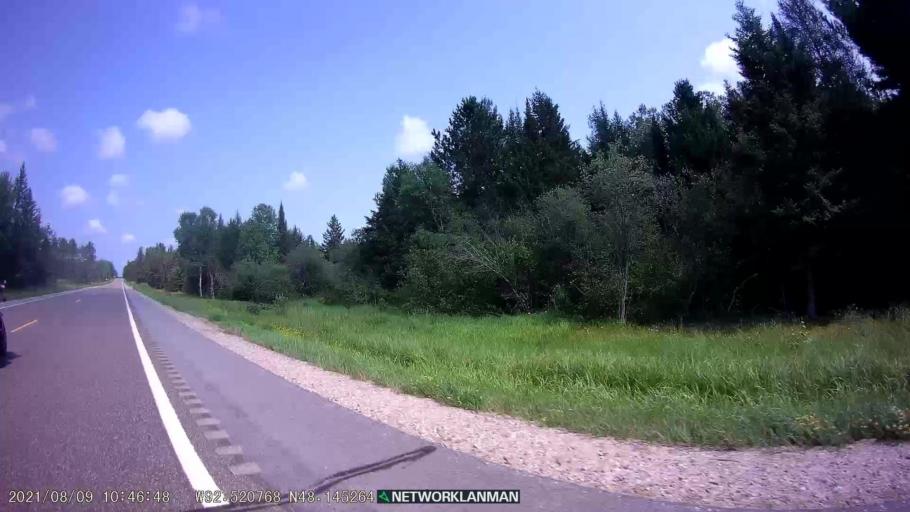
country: US
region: Minnesota
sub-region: Saint Louis County
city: Parkville
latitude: 48.1458
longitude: -92.5211
